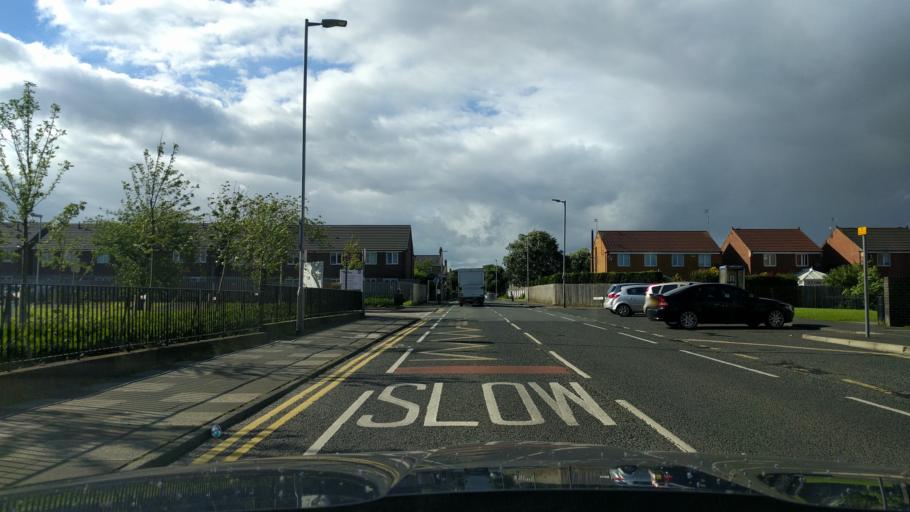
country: GB
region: England
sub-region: Northumberland
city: Ashington
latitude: 55.1737
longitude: -1.5567
